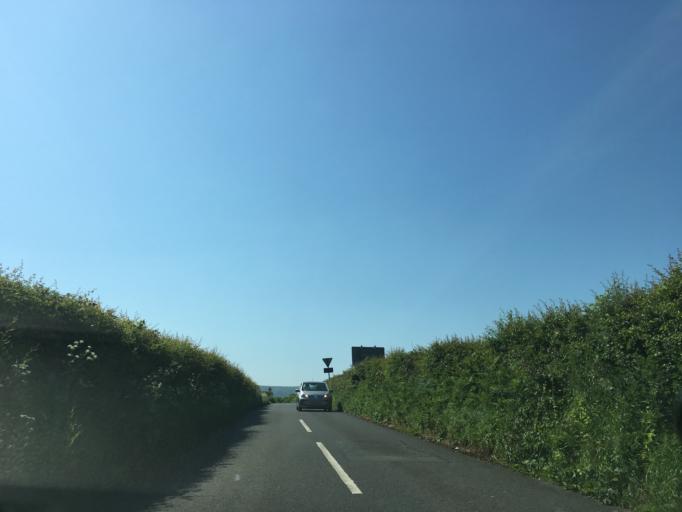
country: GB
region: England
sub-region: Isle of Wight
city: Newchurch
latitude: 50.6479
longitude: -1.2107
